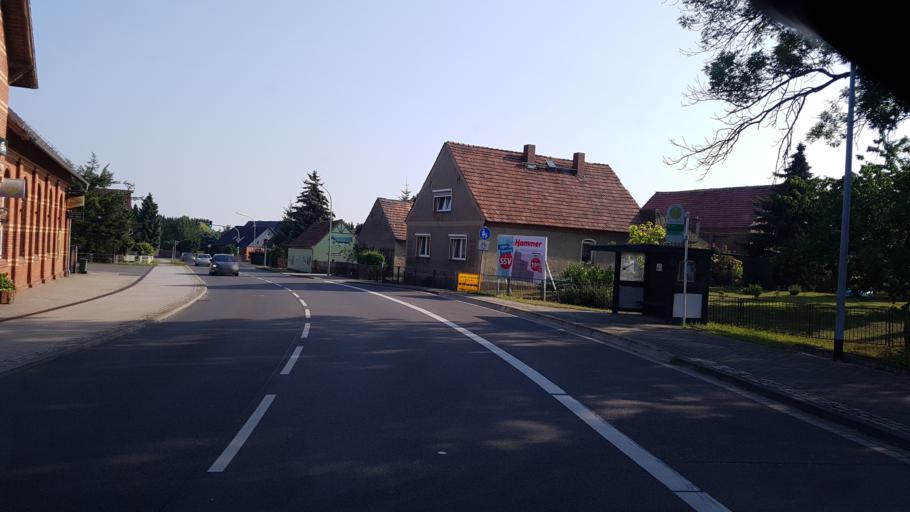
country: DE
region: Brandenburg
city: Kolkwitz
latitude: 51.6980
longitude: 14.2791
